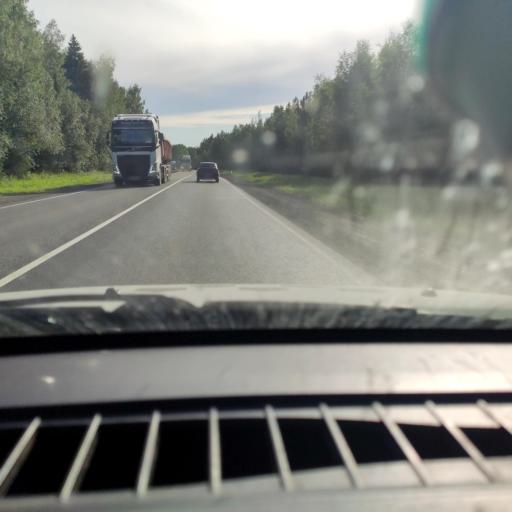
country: RU
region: Kirov
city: Vakhrushi
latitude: 58.6556
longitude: 49.8996
